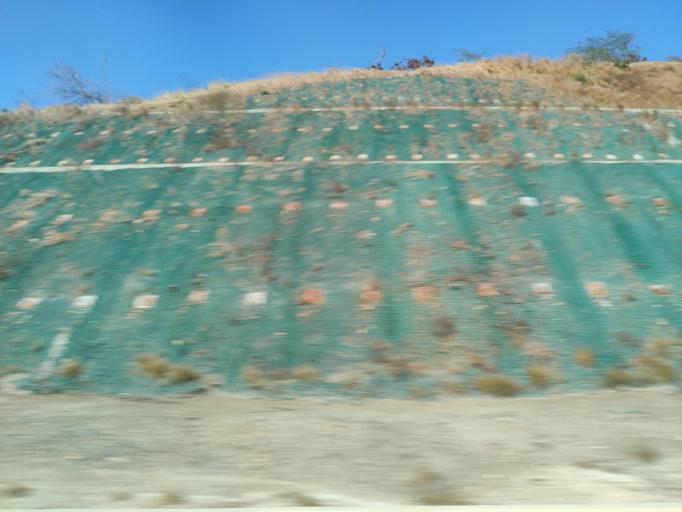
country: CO
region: Atlantico
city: Puerto Colombia
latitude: 10.9494
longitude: -75.0034
